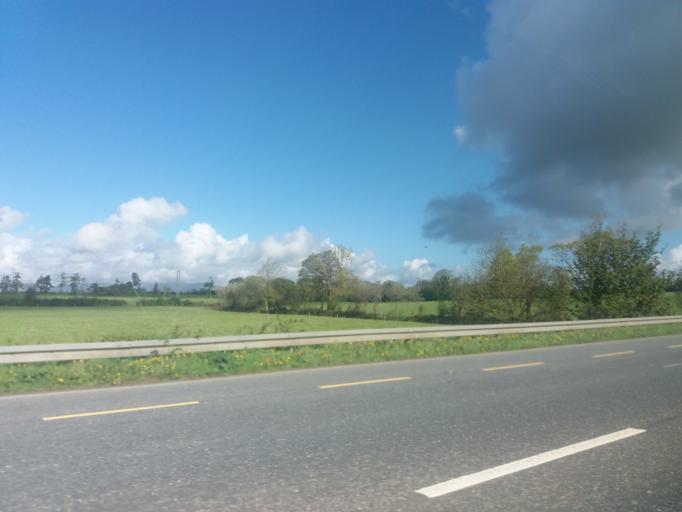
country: IE
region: Leinster
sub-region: Loch Garman
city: Enniscorthy
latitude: 52.5214
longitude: -6.5636
